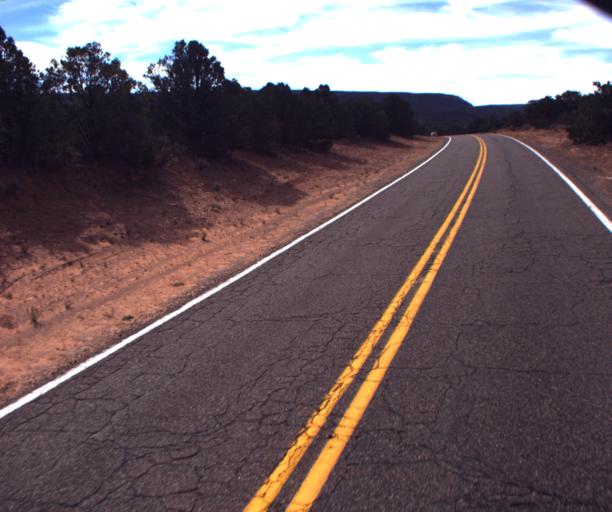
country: US
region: Arizona
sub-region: Navajo County
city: Kayenta
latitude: 36.5685
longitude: -110.5007
